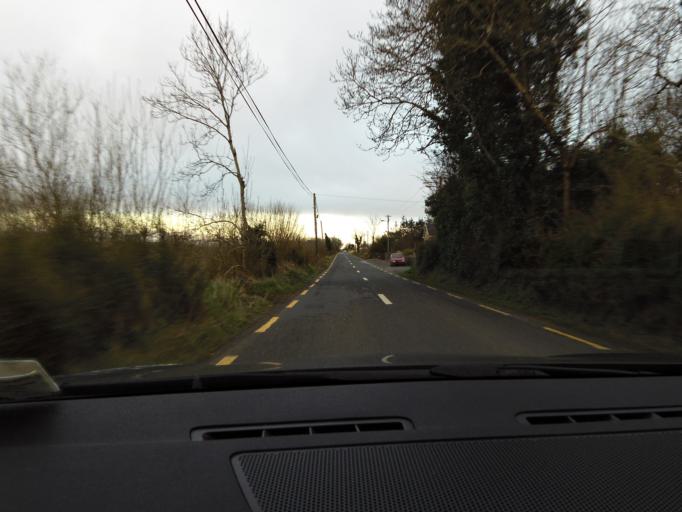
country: IE
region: Connaught
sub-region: Sligo
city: Ballymote
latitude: 53.9902
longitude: -8.5041
